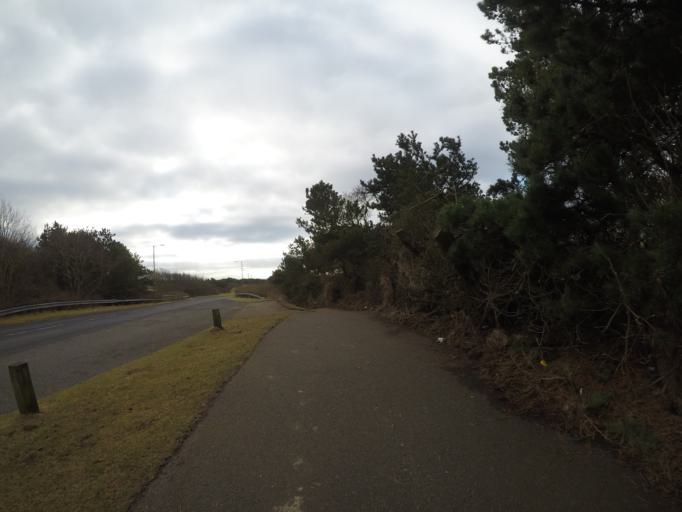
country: GB
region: Scotland
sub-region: North Ayrshire
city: Irvine
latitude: 55.6017
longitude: -4.6804
